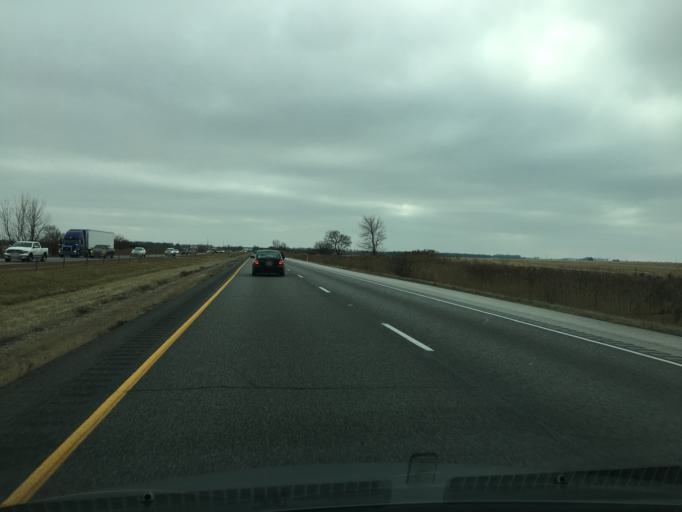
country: US
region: Indiana
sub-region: Jasper County
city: Rensselaer
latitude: 40.8958
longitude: -87.2049
